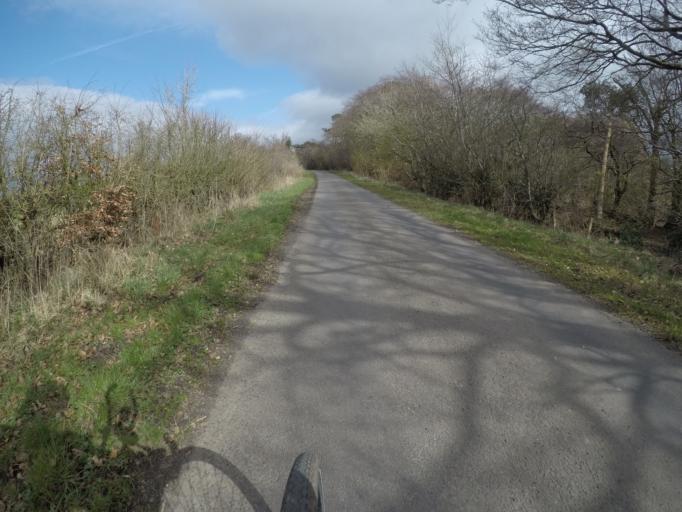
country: GB
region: Scotland
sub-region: North Ayrshire
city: Springside
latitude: 55.6514
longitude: -4.6143
